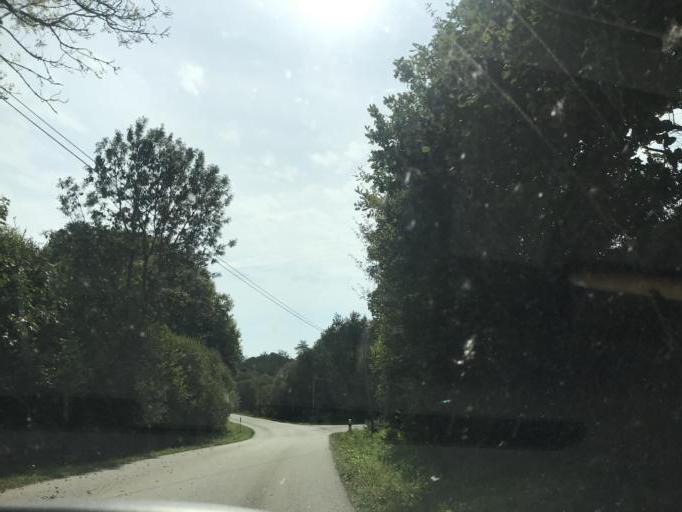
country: FR
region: Brittany
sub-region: Departement du Finistere
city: Loperec
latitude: 48.2990
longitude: -4.0185
